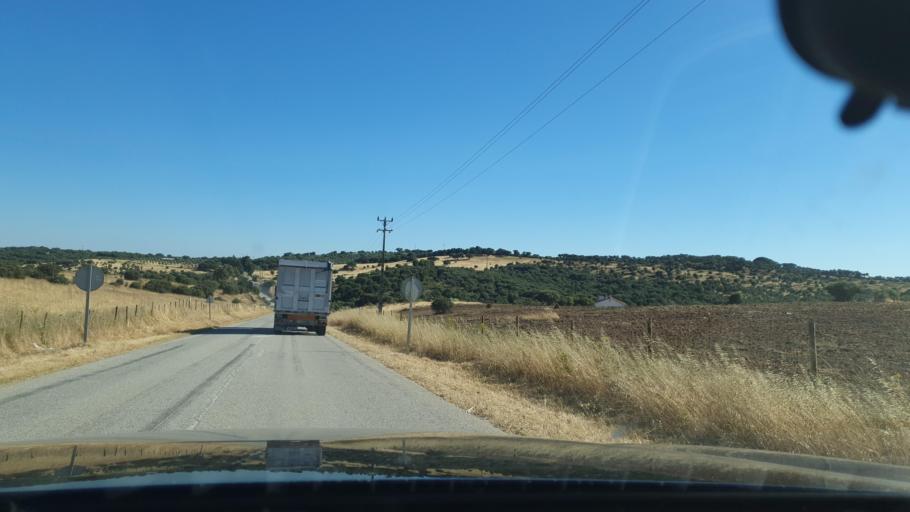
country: PT
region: Evora
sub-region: Alandroal
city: Alandroal
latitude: 38.7242
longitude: -7.4058
